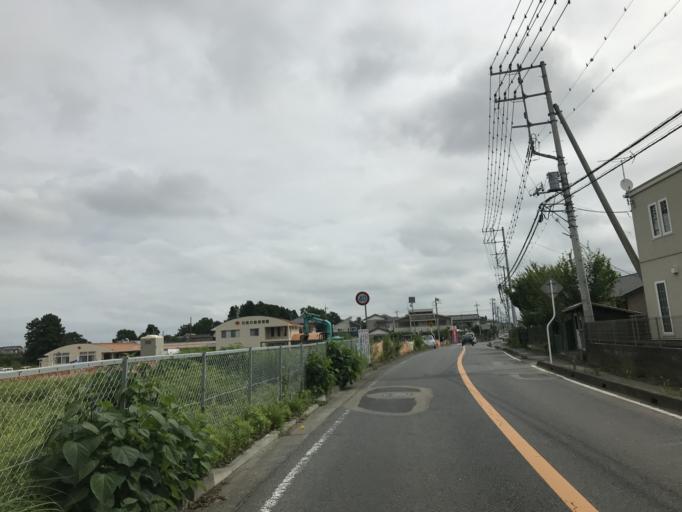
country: JP
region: Ibaraki
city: Mito-shi
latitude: 36.3274
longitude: 140.4513
